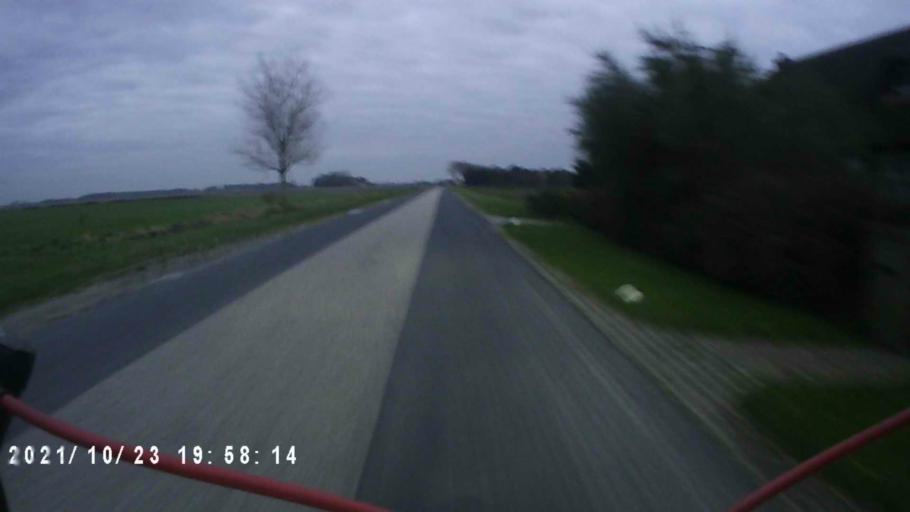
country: NL
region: Friesland
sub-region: Gemeente Harlingen
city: Harlingen
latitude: 53.1131
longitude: 5.4506
